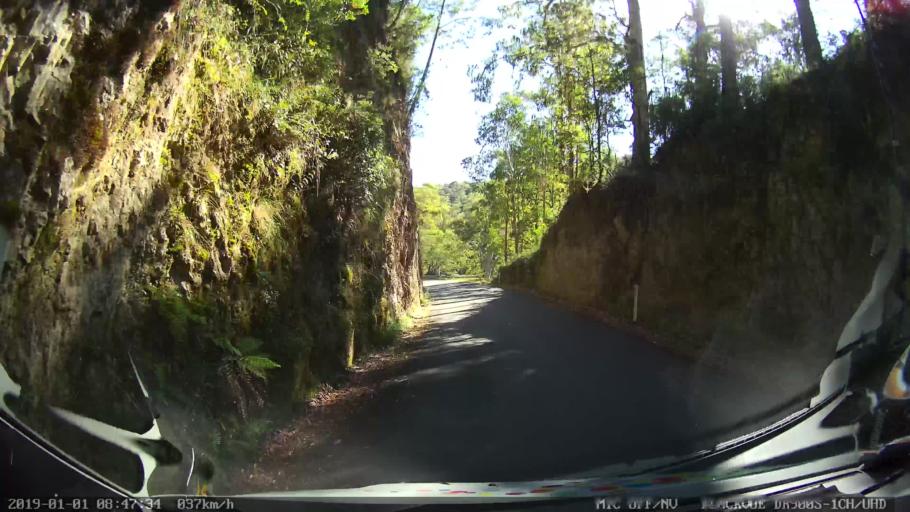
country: AU
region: New South Wales
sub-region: Snowy River
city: Jindabyne
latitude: -36.2936
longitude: 148.1976
